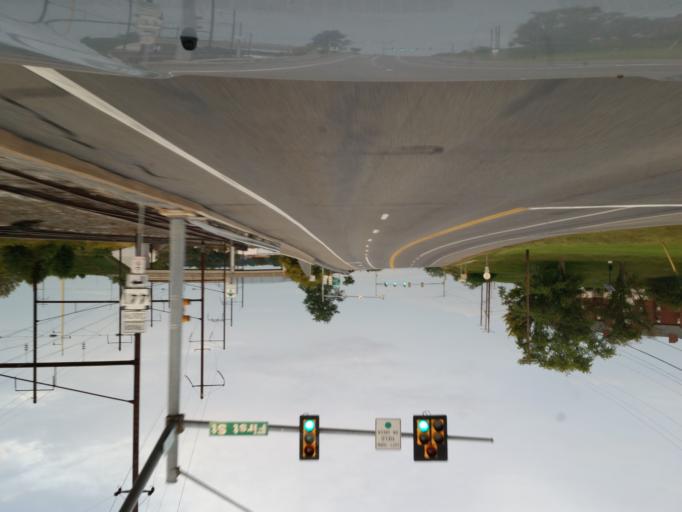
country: US
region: Pennsylvania
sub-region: Dauphin County
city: Middletown
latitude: 40.1966
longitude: -76.7416
